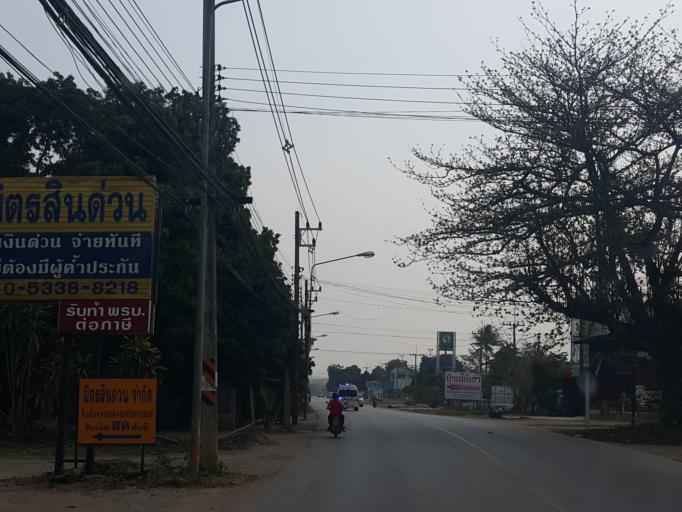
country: TH
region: Chiang Mai
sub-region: Amphoe Chiang Dao
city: Chiang Dao
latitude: 19.3633
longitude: 98.9644
